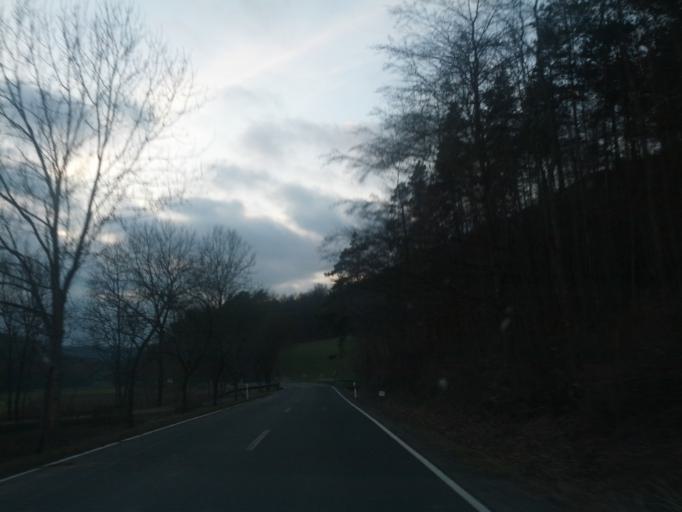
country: DE
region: Thuringia
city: Treffurt
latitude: 51.1465
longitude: 10.2348
